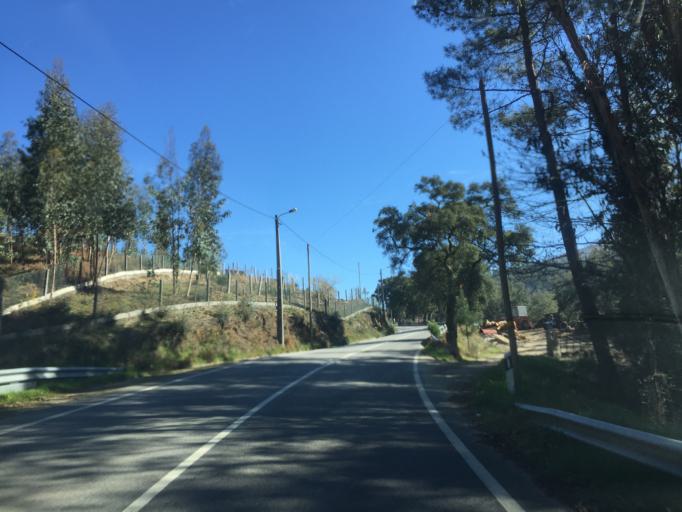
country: PT
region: Aveiro
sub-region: Vale de Cambra
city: Macieira de Cambra
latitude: 40.8886
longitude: -8.3494
